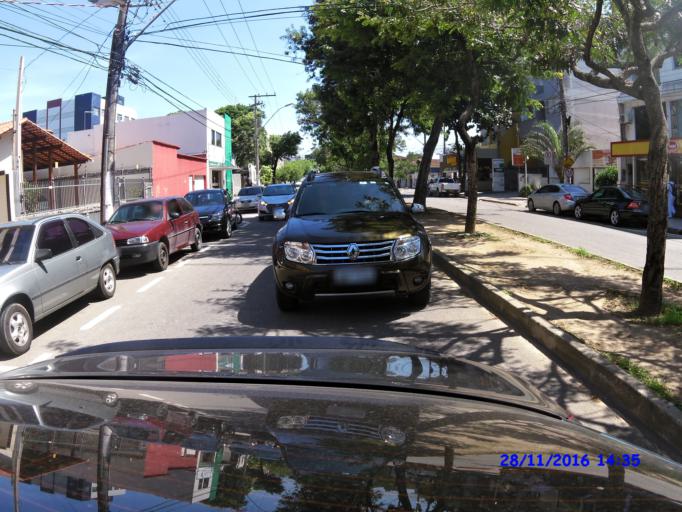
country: BR
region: Espirito Santo
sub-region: Vila Velha
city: Vila Velha
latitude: -20.2560
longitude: -40.2670
